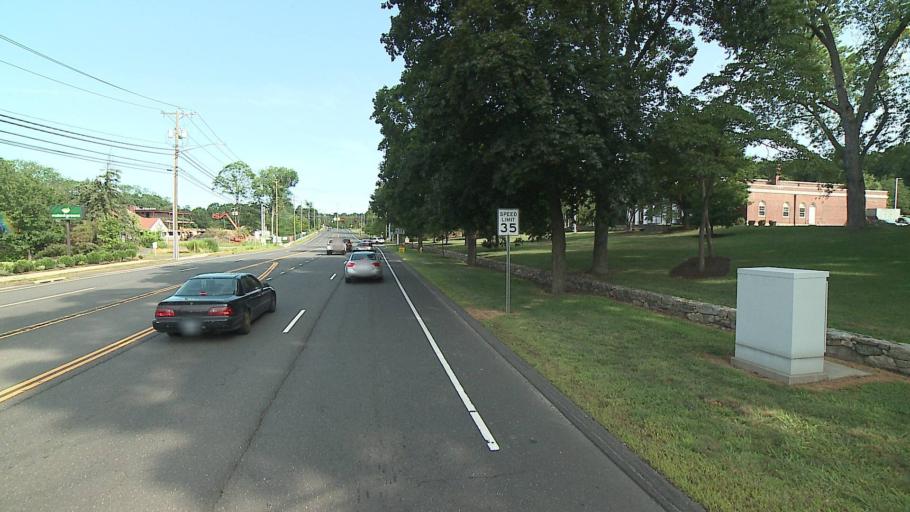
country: US
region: Connecticut
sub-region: Fairfield County
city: Wilton
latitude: 41.1894
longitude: -73.4262
